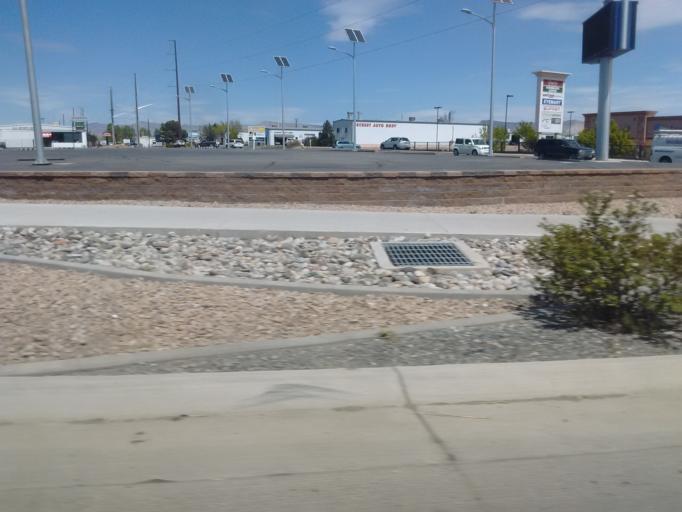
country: US
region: Colorado
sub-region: Mesa County
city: Grand Junction
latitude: 39.0834
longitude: -108.5898
